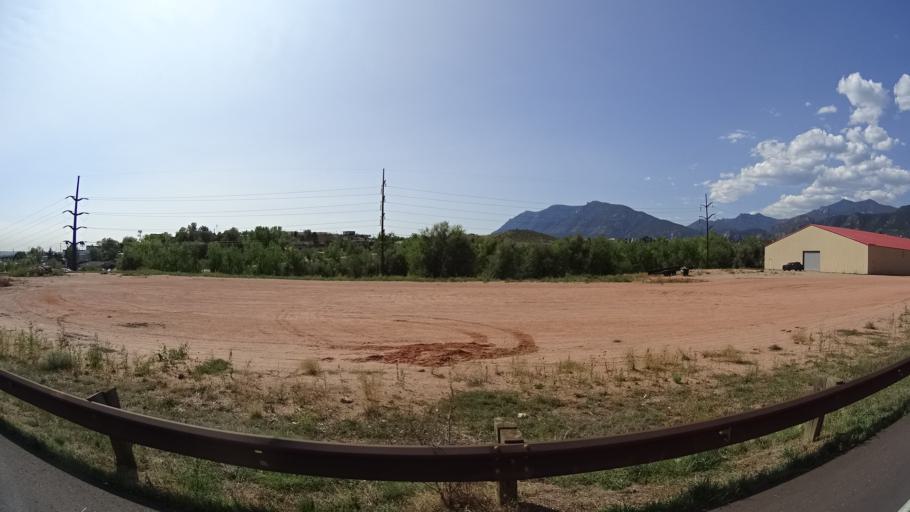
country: US
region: Colorado
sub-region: El Paso County
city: Colorado Springs
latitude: 38.8228
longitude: -104.8433
